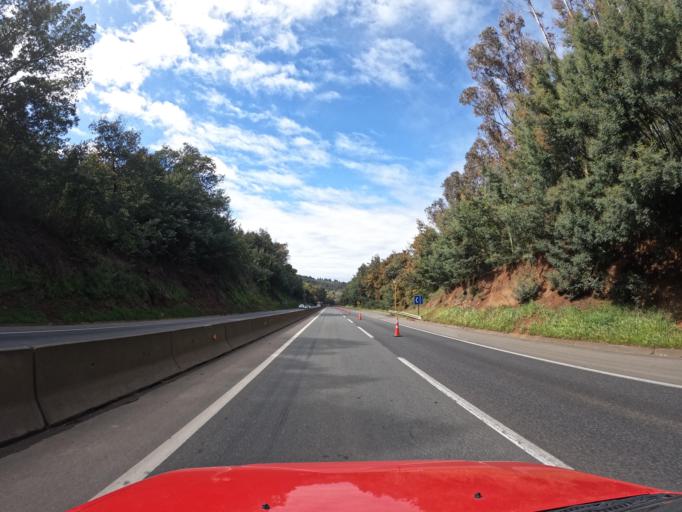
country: CL
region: Araucania
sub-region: Provincia de Malleco
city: Collipulli
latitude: -37.8409
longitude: -72.3890
